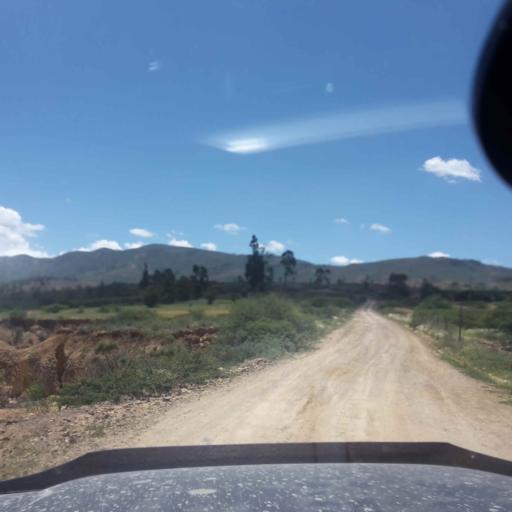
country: BO
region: Cochabamba
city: Totora
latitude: -17.7748
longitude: -65.2467
